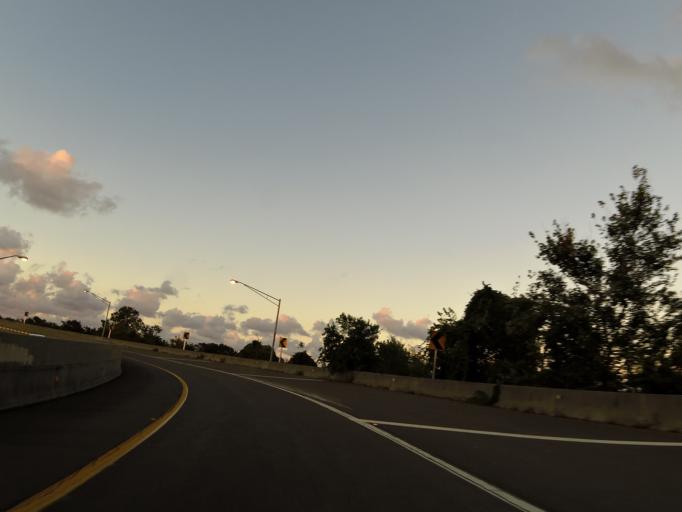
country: US
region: Florida
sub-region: Saint Johns County
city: Ponte Vedra Beach
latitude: 30.2545
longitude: -81.3868
